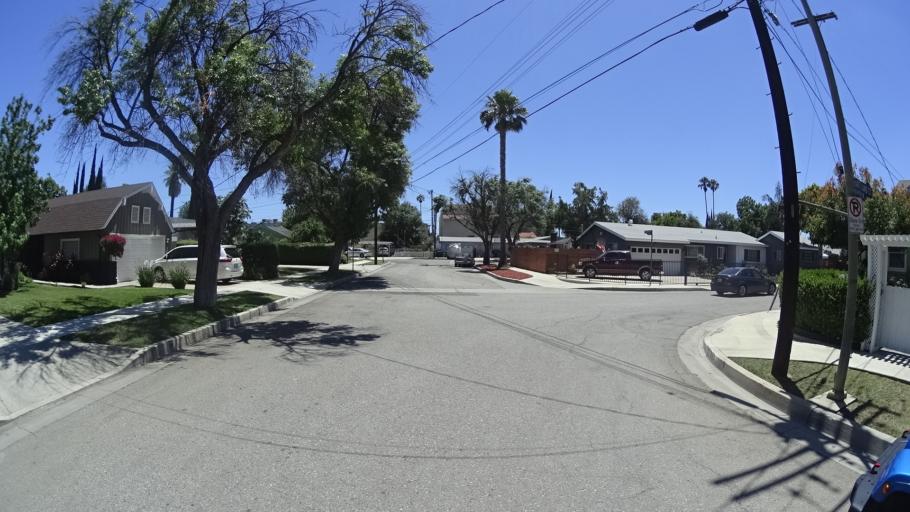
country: US
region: California
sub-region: Los Angeles County
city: Van Nuys
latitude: 34.1955
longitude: -118.4695
